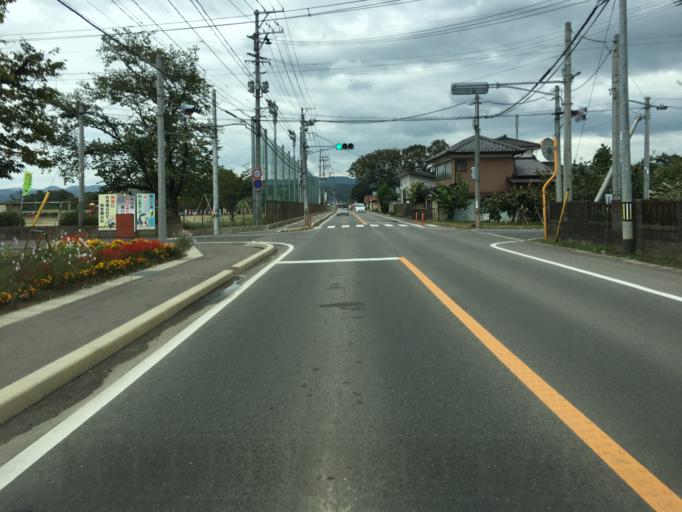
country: JP
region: Fukushima
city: Yanagawamachi-saiwaicho
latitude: 37.8496
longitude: 140.5801
